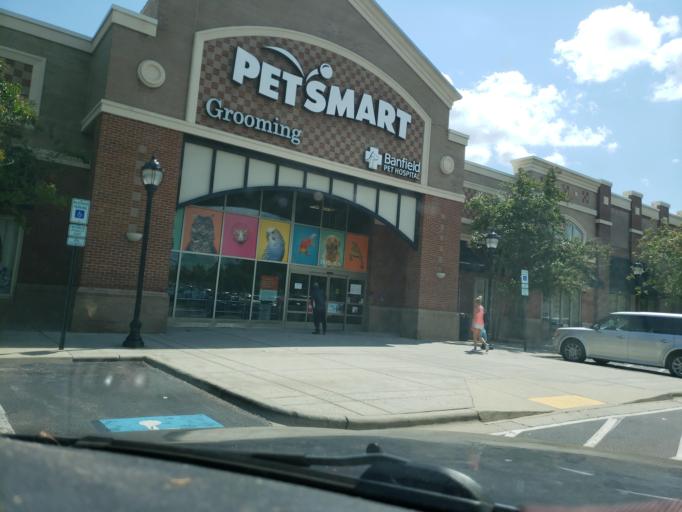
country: US
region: North Carolina
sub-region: Orange County
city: Chapel Hill
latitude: 35.9497
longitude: -78.9878
